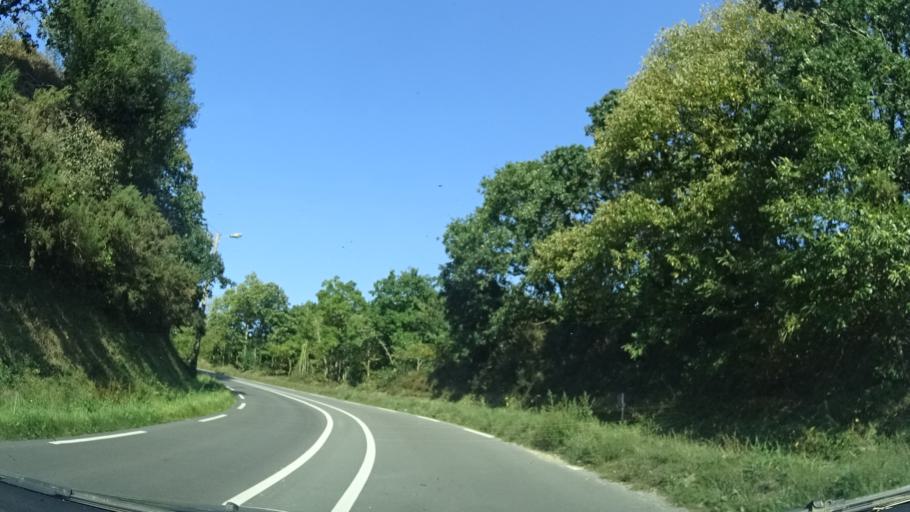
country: FR
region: Brittany
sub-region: Departement du Finistere
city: Douarnenez
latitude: 48.0814
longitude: -4.3307
